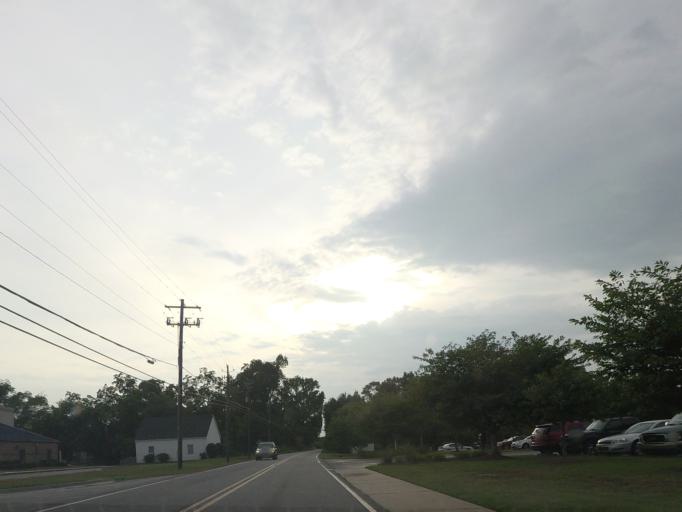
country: US
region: Georgia
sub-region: Houston County
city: Centerville
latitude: 32.7169
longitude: -83.6900
